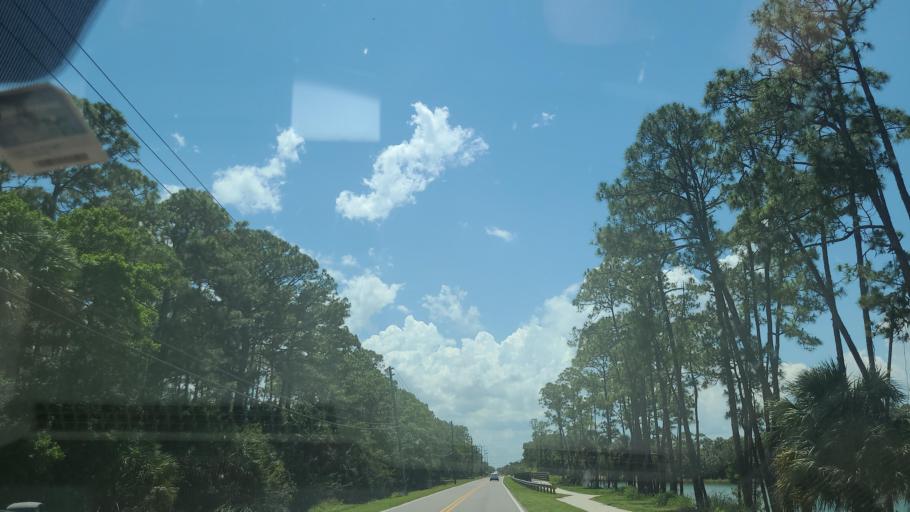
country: US
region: Florida
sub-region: Brevard County
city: Grant-Valkaria
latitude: 27.9537
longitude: -80.5859
